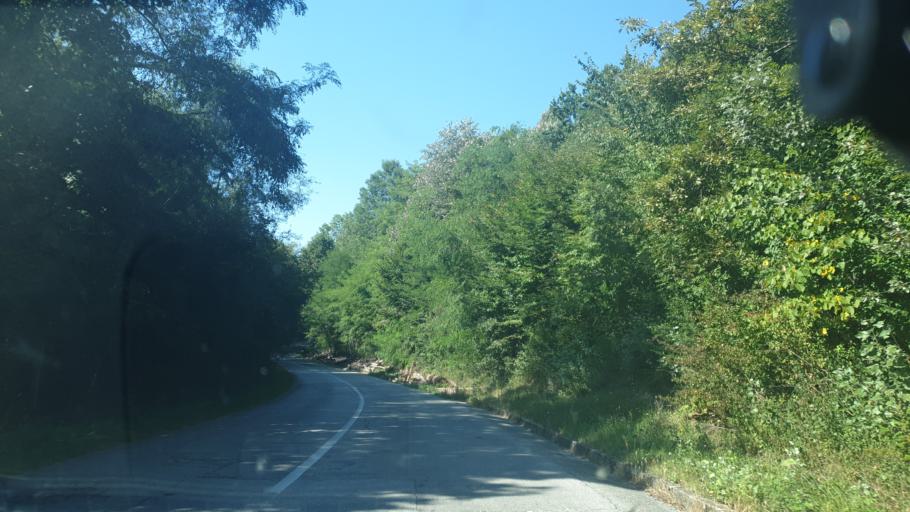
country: RS
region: Central Serbia
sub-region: Kolubarski Okrug
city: Lajkovac
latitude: 44.3219
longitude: 20.1888
